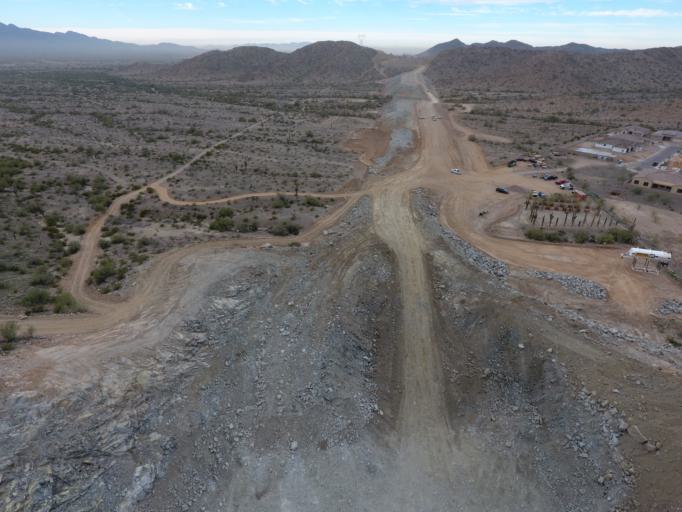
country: US
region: Arizona
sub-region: Maricopa County
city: Laveen
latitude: 33.2963
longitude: -112.1375
